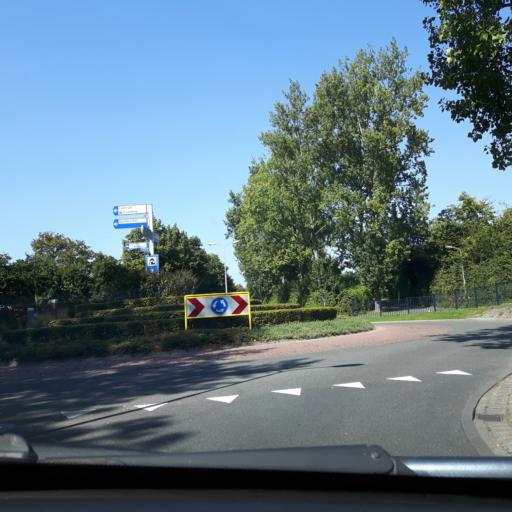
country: NL
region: Zeeland
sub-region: Gemeente Reimerswaal
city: Yerseke
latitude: 51.4868
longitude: 4.0490
